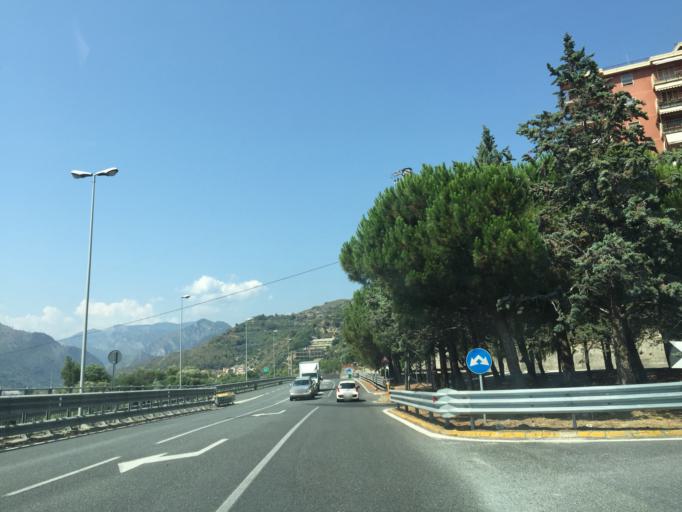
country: IT
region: Liguria
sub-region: Provincia di Imperia
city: Ventimiglia
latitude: 43.8093
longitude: 7.5923
